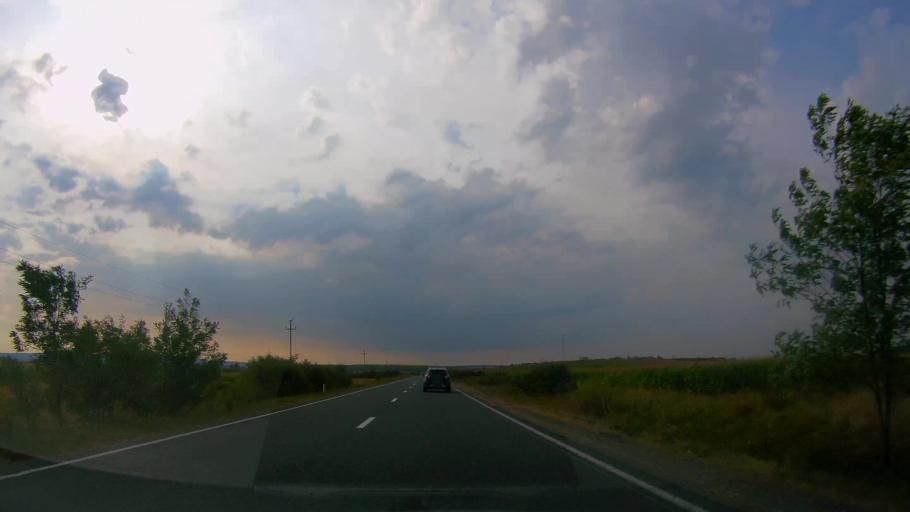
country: RO
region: Satu Mare
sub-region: Oras Ardud
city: Ardud
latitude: 47.6192
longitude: 22.8732
